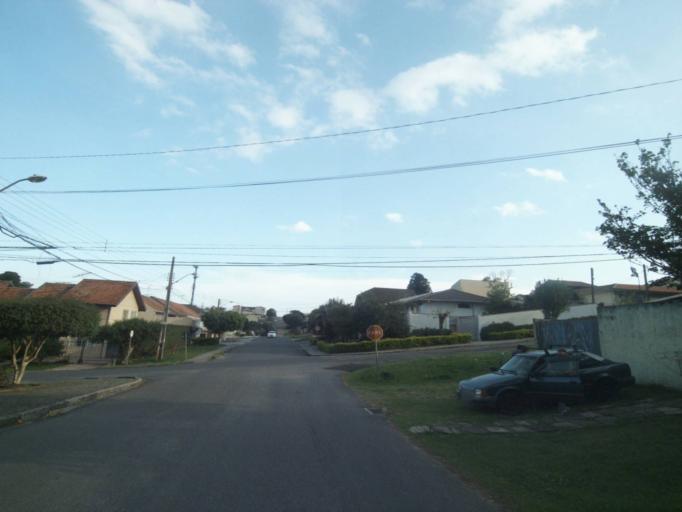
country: BR
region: Parana
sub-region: Pinhais
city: Pinhais
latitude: -25.3979
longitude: -49.2054
